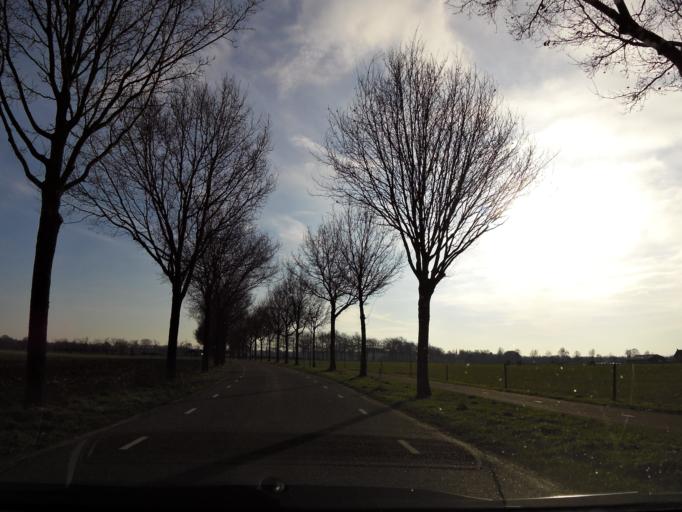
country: NL
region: Limburg
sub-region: Gemeente Beesel
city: Beesel
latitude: 51.2489
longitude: 6.0304
